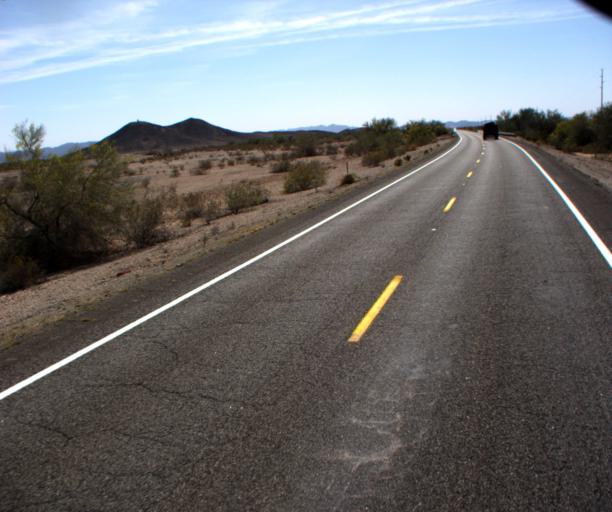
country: US
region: Arizona
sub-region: Yuma County
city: Fortuna Foothills
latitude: 32.9418
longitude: -114.3055
